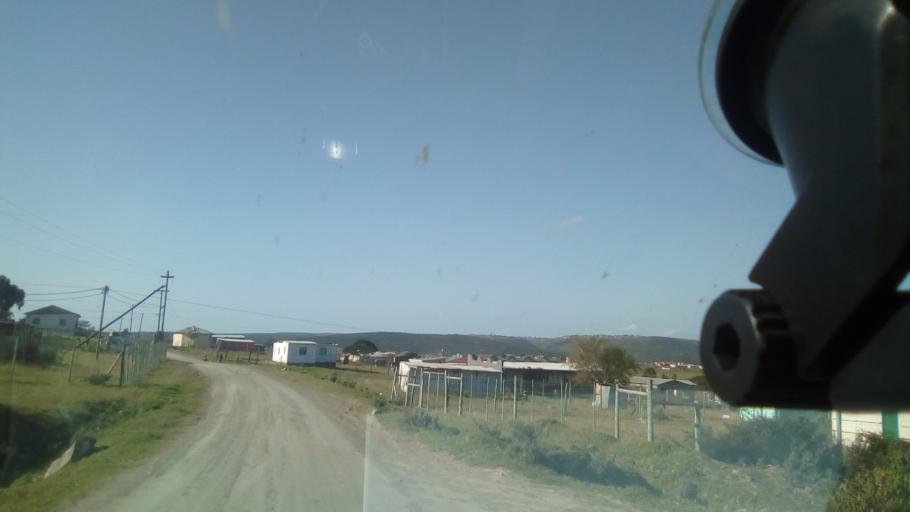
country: ZA
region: Eastern Cape
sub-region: Buffalo City Metropolitan Municipality
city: Bhisho
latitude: -32.8134
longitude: 27.3548
